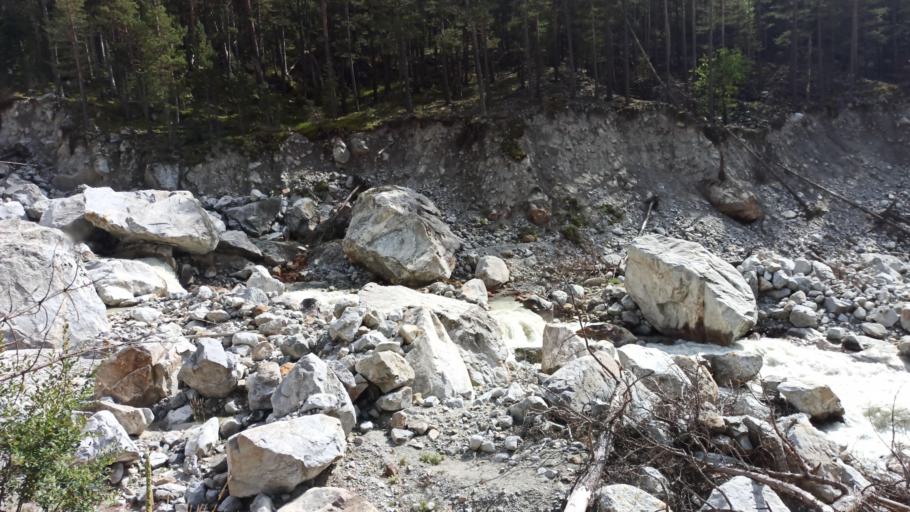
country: RU
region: Kabardino-Balkariya
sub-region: El'brusskiy Rayon
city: El'brus
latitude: 43.2197
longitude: 42.6889
